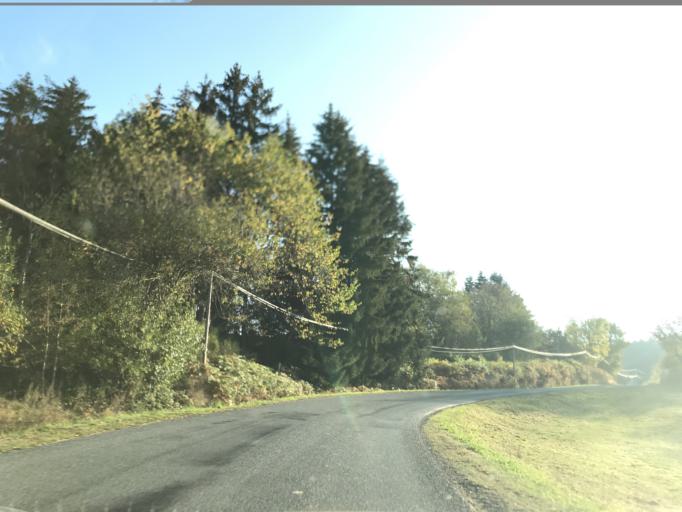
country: FR
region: Rhone-Alpes
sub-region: Departement de la Loire
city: Noiretable
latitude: 45.8116
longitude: 3.7472
